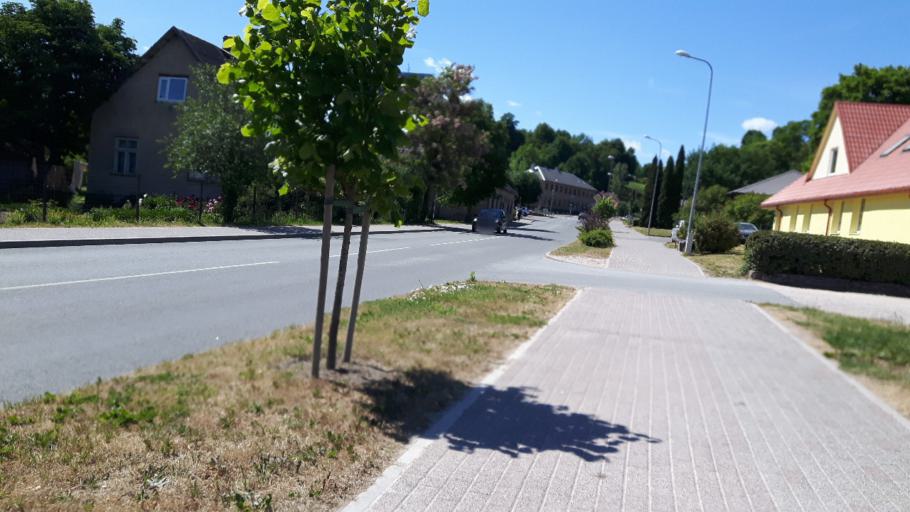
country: LV
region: Kandava
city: Kandava
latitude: 57.0340
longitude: 22.7830
